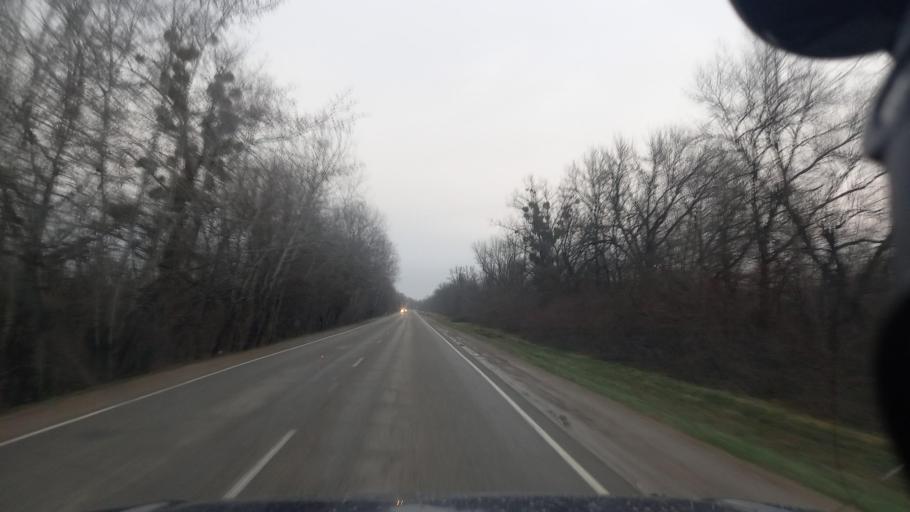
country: RU
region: Krasnodarskiy
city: Saratovskaya
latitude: 44.6848
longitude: 39.2133
